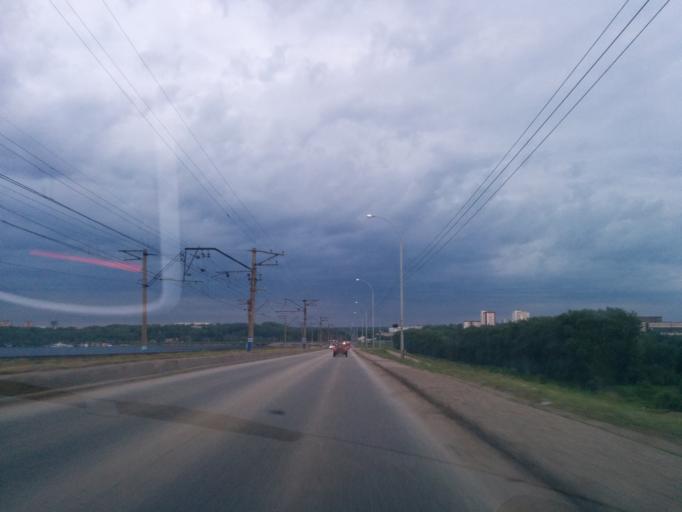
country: RU
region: Perm
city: Perm
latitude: 58.1150
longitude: 56.3482
